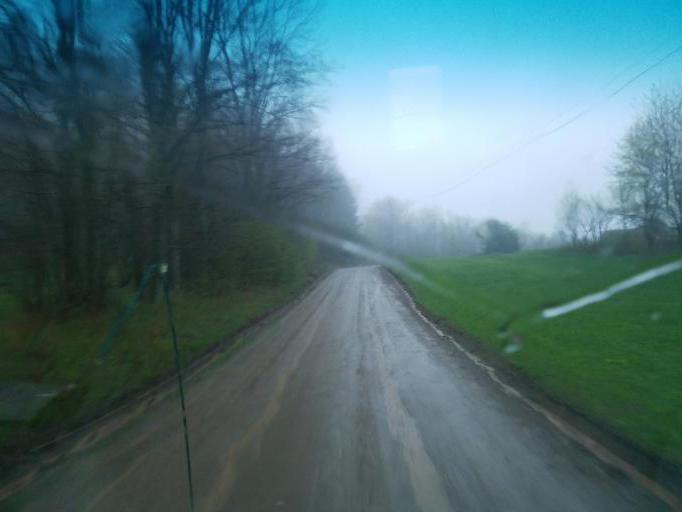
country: US
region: Pennsylvania
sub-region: Tioga County
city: Westfield
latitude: 41.9293
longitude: -77.7225
